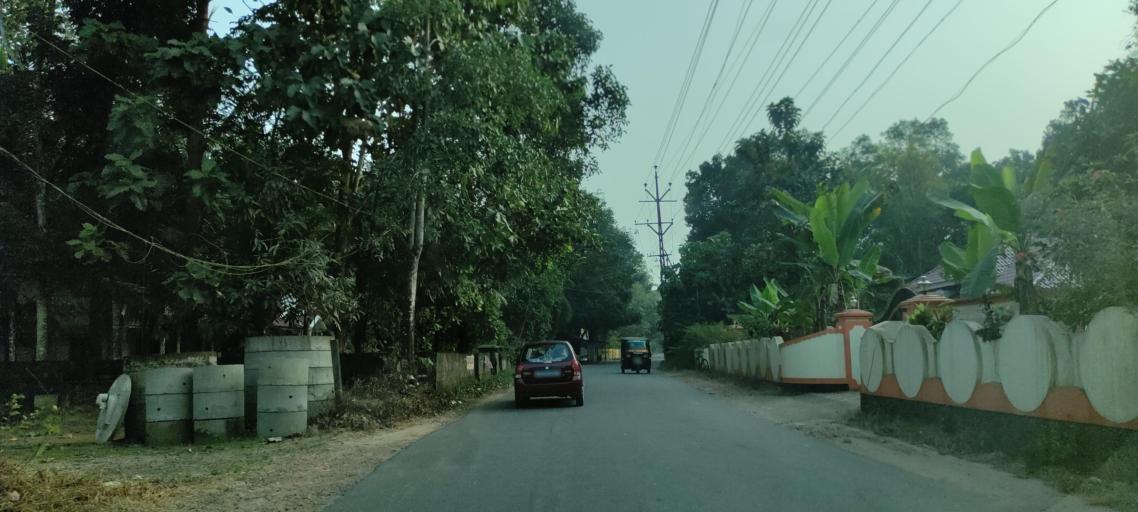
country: IN
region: Kerala
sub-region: Kottayam
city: Vaikam
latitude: 9.7130
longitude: 76.4756
